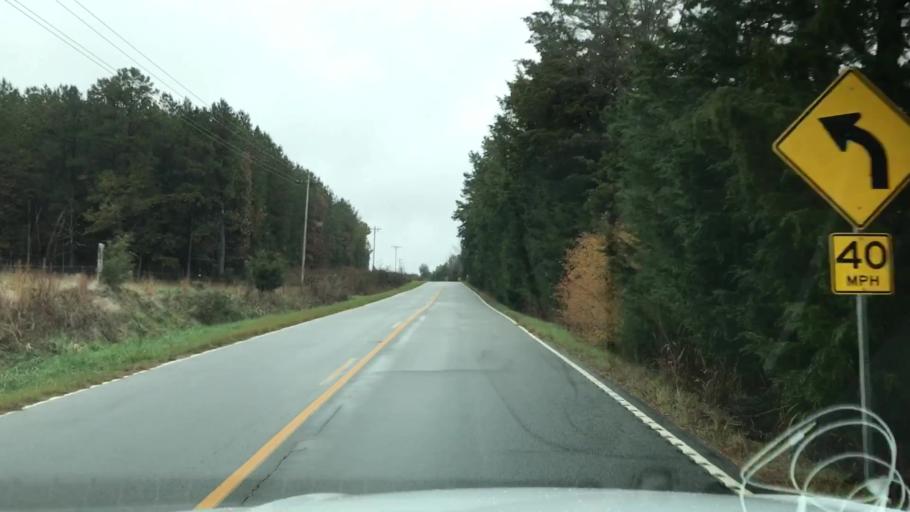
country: US
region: South Carolina
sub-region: Spartanburg County
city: Woodruff
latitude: 34.7625
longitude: -81.9161
